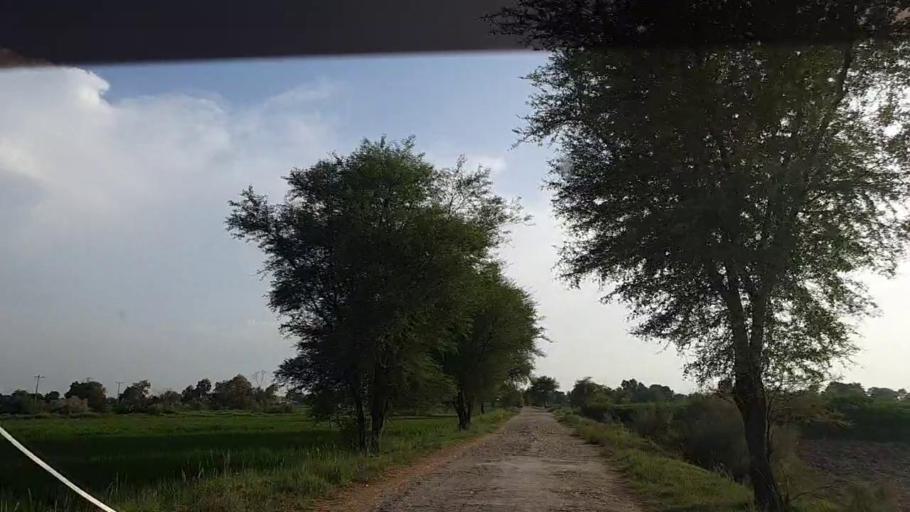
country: PK
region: Sindh
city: Khanpur
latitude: 27.8227
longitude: 69.3421
